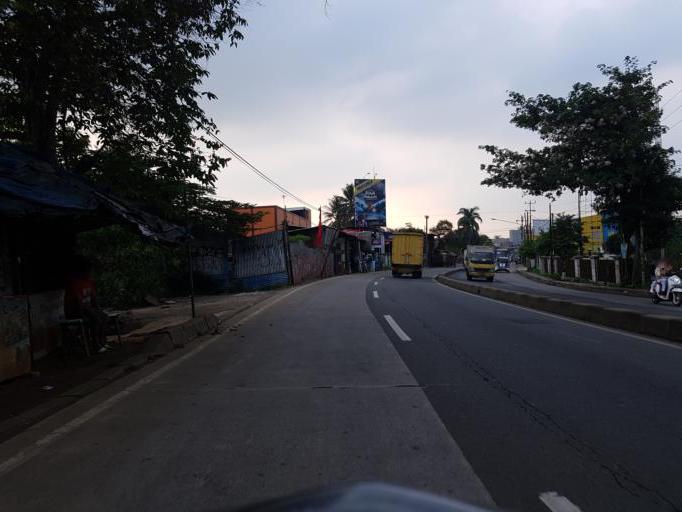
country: ID
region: West Java
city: Parung
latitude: -6.4842
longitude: 106.7334
